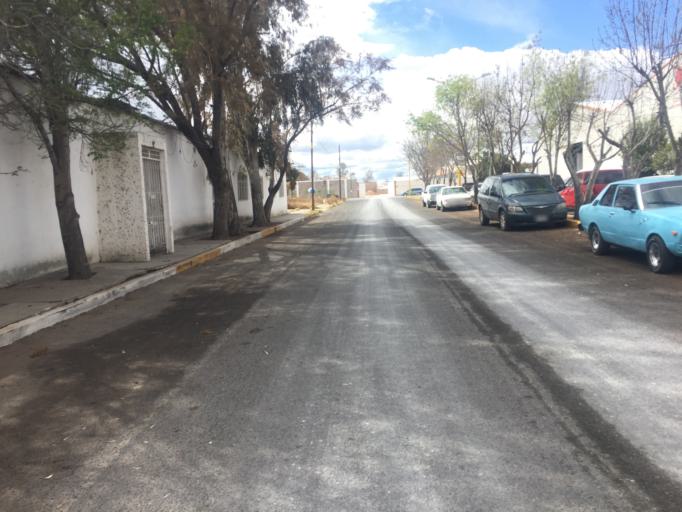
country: MX
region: Durango
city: Victoria de Durango
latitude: 24.0663
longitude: -104.6057
